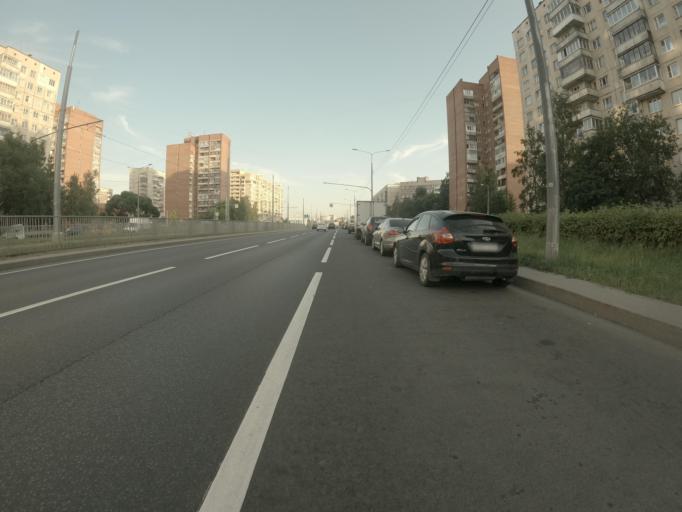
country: RU
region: St.-Petersburg
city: Krasnogvargeisky
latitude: 59.9394
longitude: 30.4889
